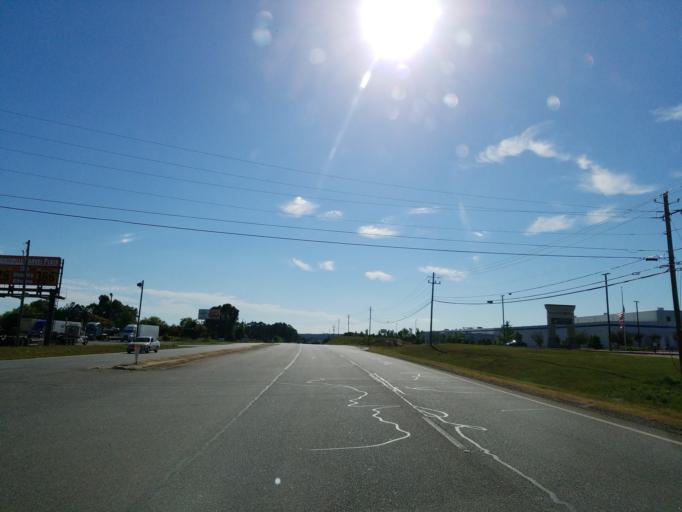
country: US
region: Georgia
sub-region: Bartow County
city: Adairsville
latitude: 34.3770
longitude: -84.9185
